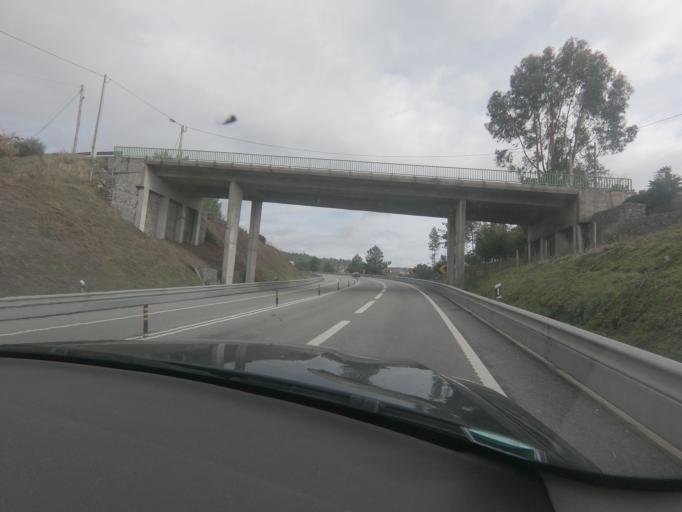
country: PT
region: Vila Real
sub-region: Vila Real
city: Vila Real
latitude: 41.3155
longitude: -7.7171
